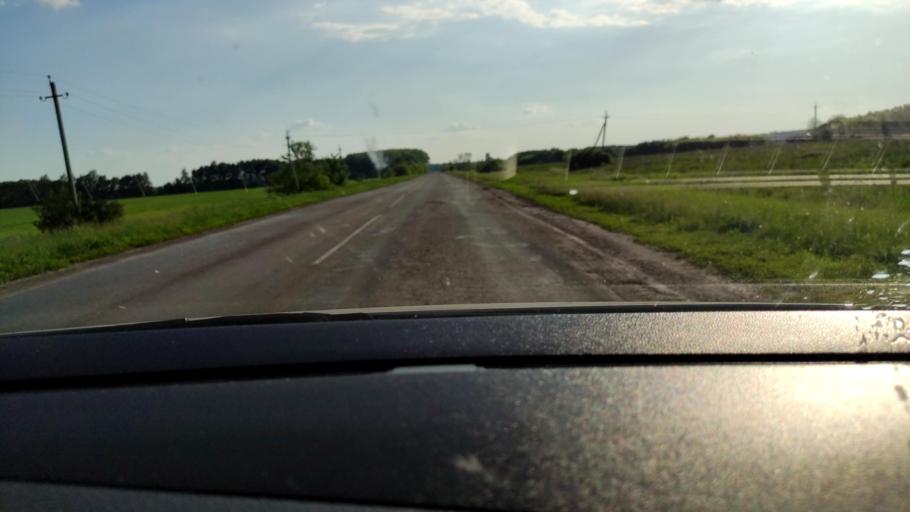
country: RU
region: Voronezj
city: Panino
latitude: 51.6080
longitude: 39.9993
